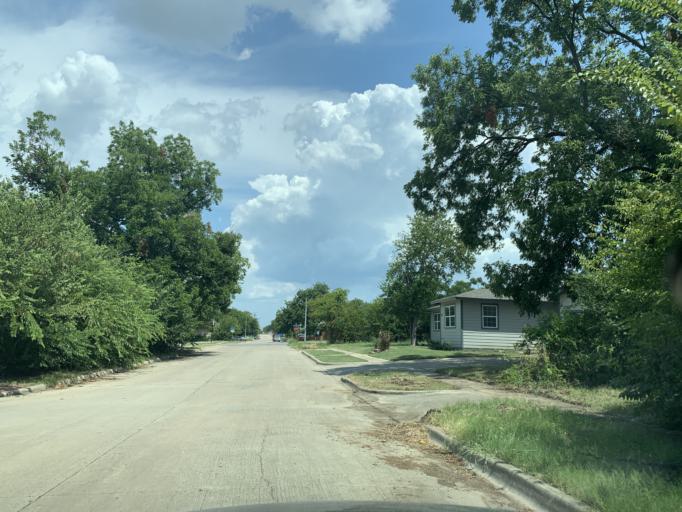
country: US
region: Texas
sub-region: Tarrant County
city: Fort Worth
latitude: 32.7270
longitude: -97.3193
